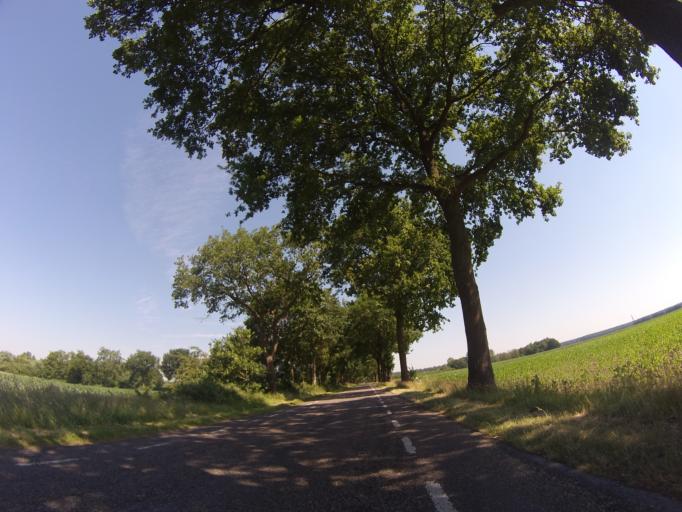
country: NL
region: Drenthe
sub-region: Gemeente Coevorden
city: Sleen
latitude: 52.8095
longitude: 6.7393
